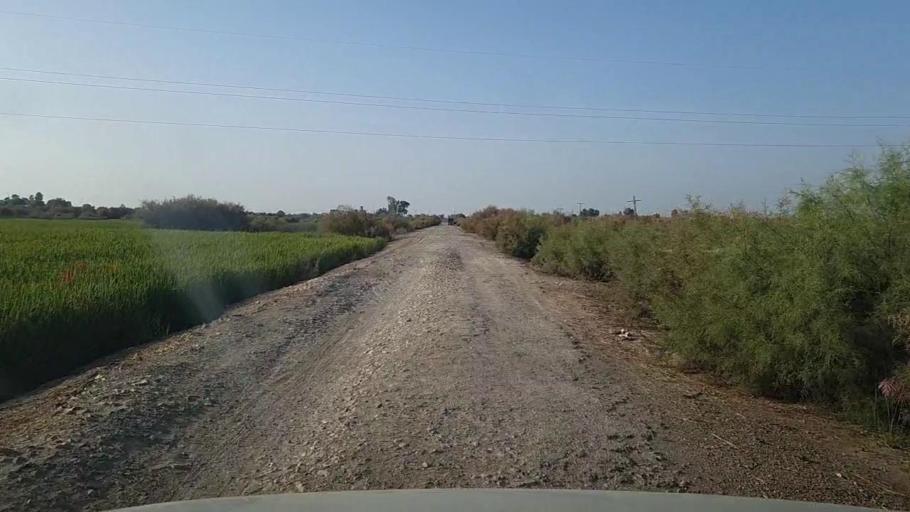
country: PK
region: Sindh
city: Kandhkot
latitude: 28.3081
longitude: 69.3282
